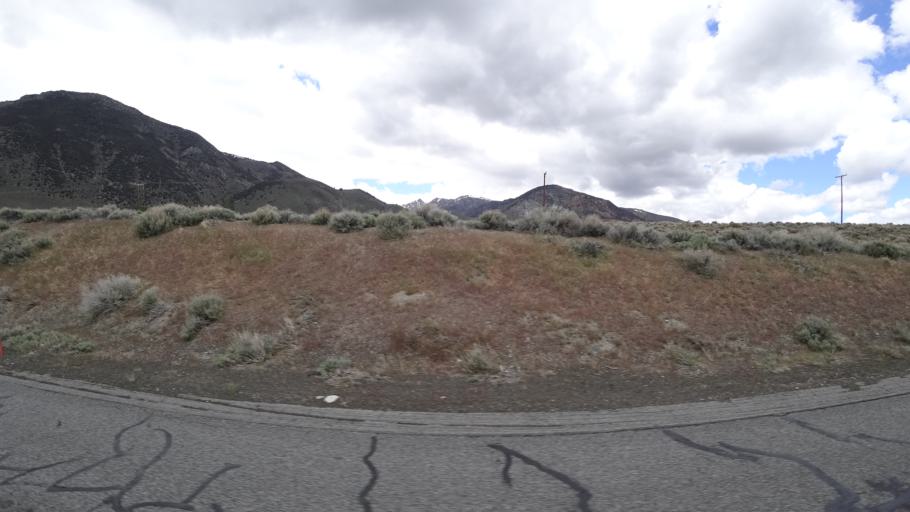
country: US
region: California
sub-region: Mono County
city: Bridgeport
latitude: 38.0248
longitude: -119.1562
